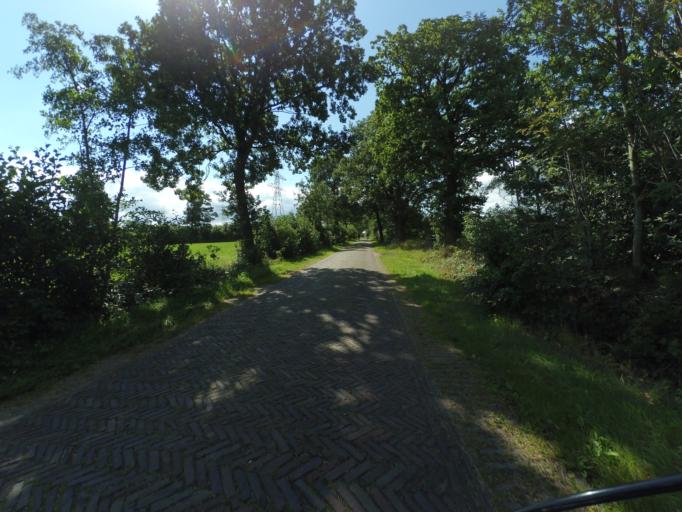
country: NL
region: Friesland
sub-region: Gemeente Achtkarspelen
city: Twijzelerheide
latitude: 53.2212
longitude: 6.0437
